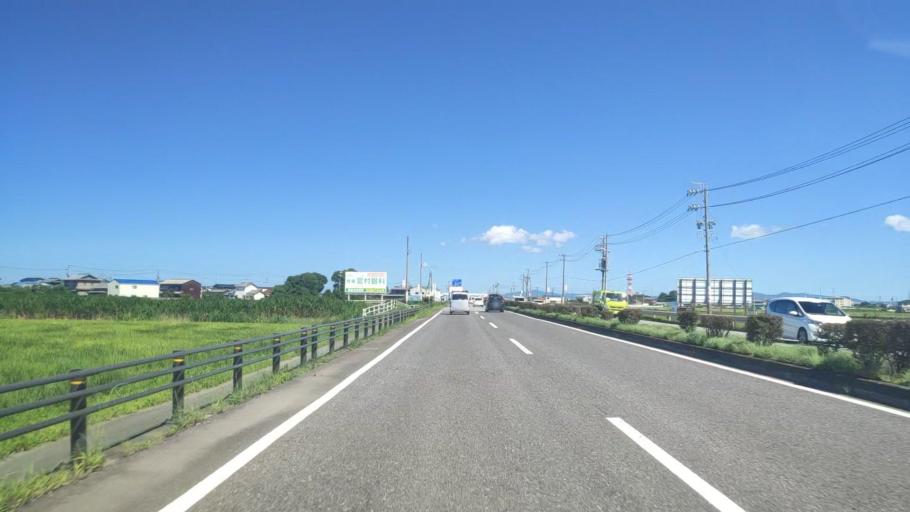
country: JP
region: Mie
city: Hisai-motomachi
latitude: 34.6003
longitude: 136.5314
